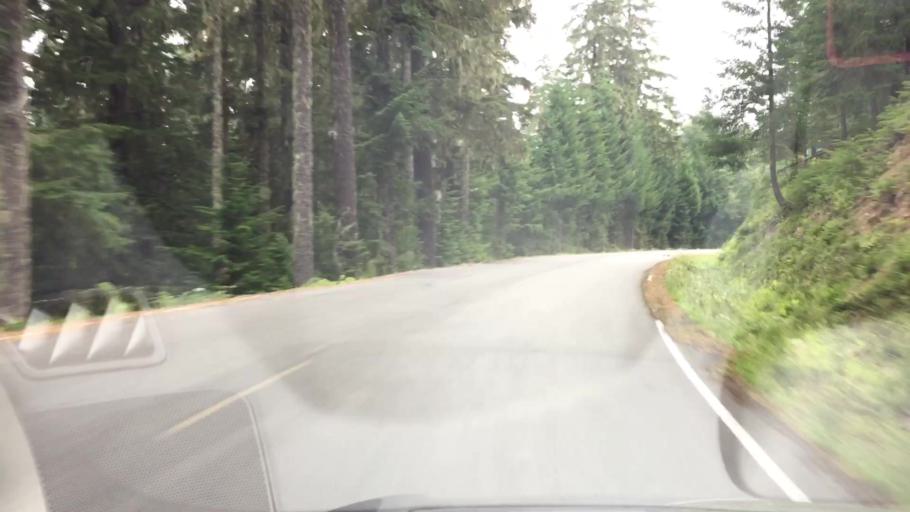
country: US
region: Washington
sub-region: Klickitat County
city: White Salmon
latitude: 46.2053
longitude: -121.6444
